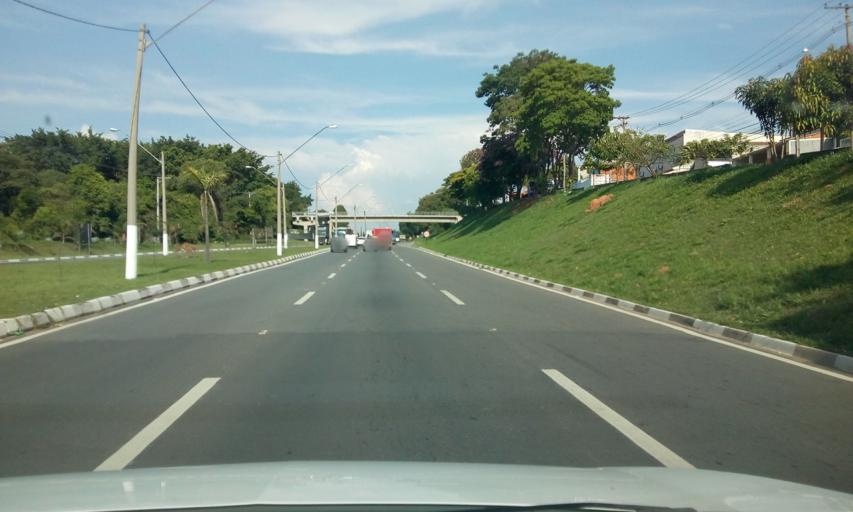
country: BR
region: Sao Paulo
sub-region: Itupeva
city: Itupeva
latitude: -23.1579
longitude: -47.0387
